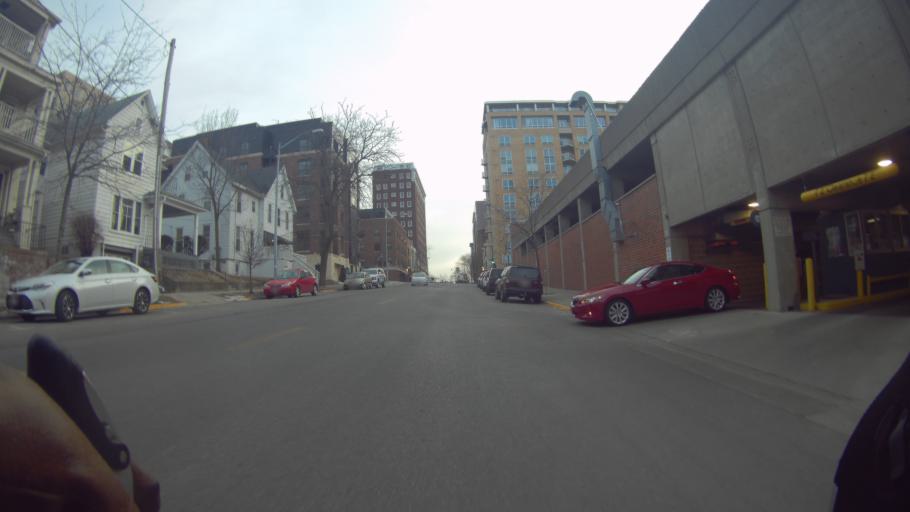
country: US
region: Wisconsin
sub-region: Dane County
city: Madison
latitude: 43.0774
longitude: -89.3825
